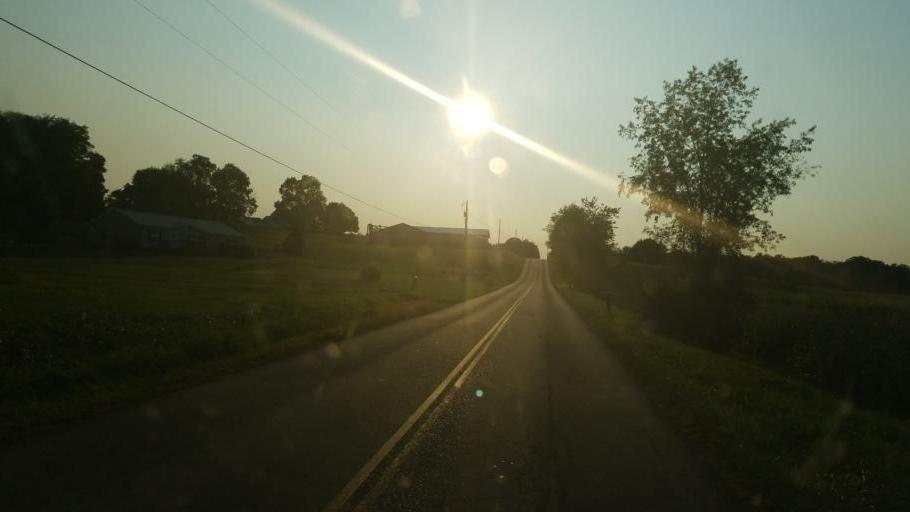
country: US
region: Ohio
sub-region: Wayne County
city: Shreve
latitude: 40.6678
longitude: -81.9752
